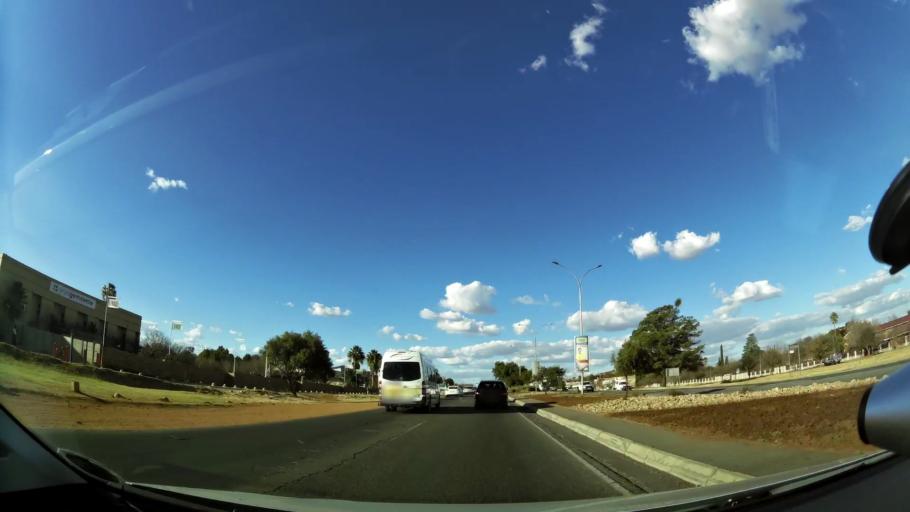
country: ZA
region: North-West
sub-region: Dr Kenneth Kaunda District Municipality
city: Klerksdorp
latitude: -26.8554
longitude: 26.6786
